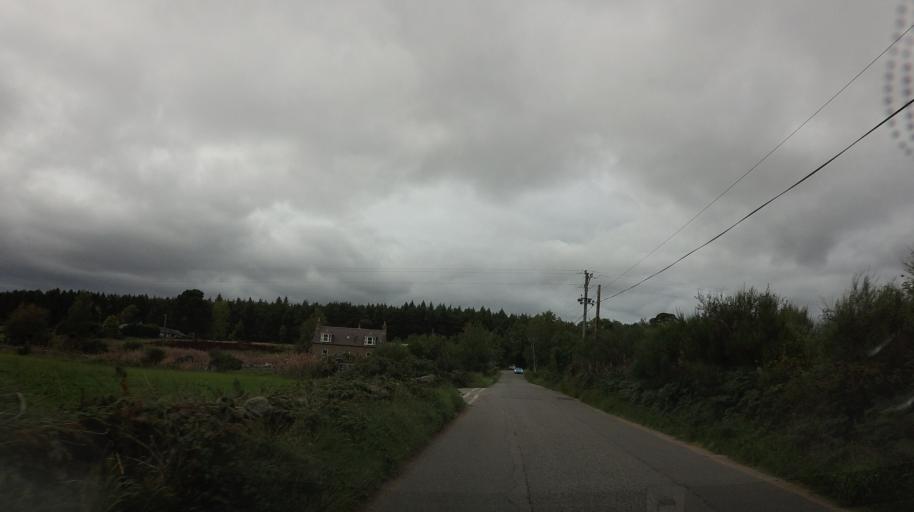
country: GB
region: Scotland
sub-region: Aberdeenshire
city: Banchory
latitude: 57.0646
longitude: -2.4689
